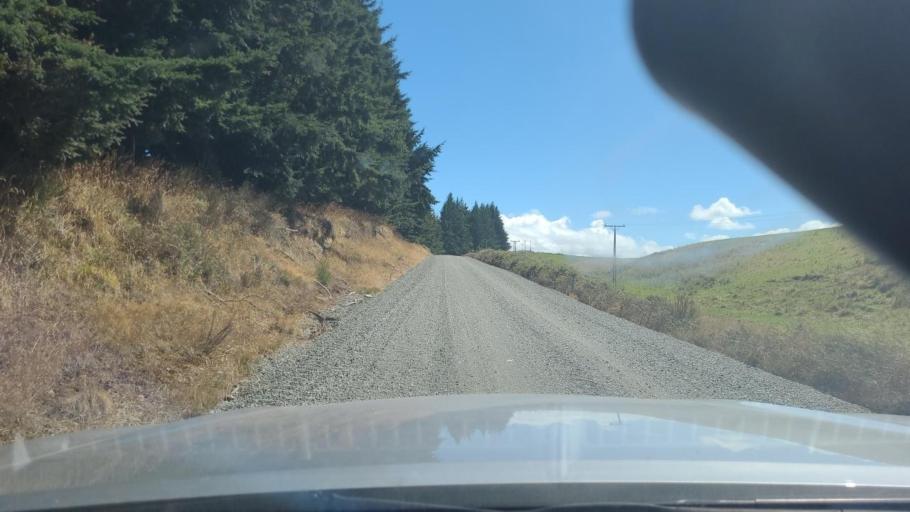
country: NZ
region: Southland
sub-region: Southland District
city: Te Anau
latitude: -45.4901
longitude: 167.8318
